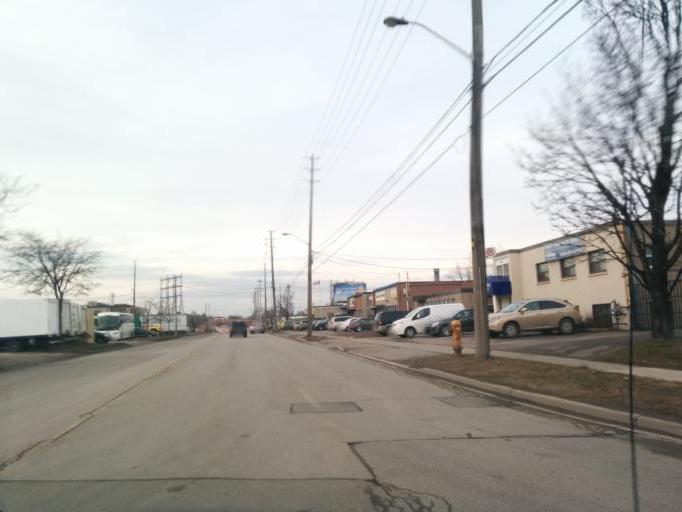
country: CA
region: Ontario
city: Etobicoke
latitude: 43.6261
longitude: -79.5422
